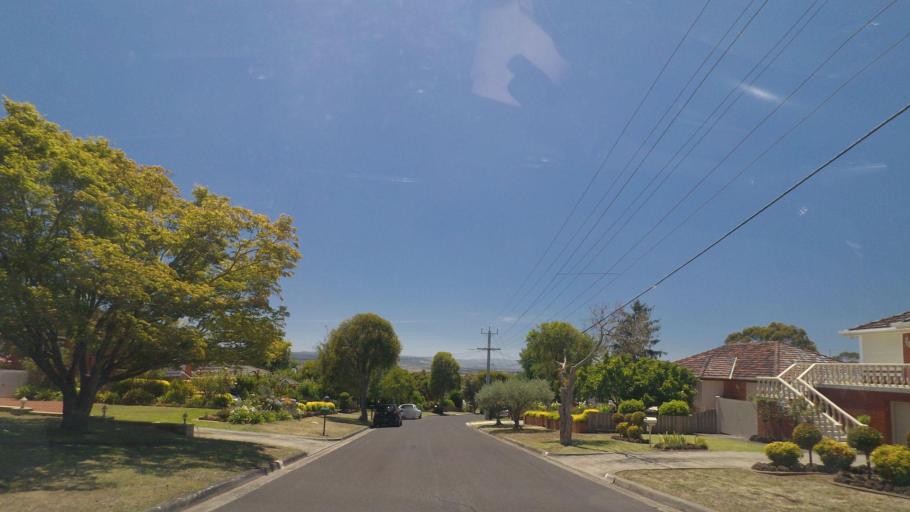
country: AU
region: Victoria
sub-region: Yarra Ranges
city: Lilydale
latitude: -37.7591
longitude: 145.3311
